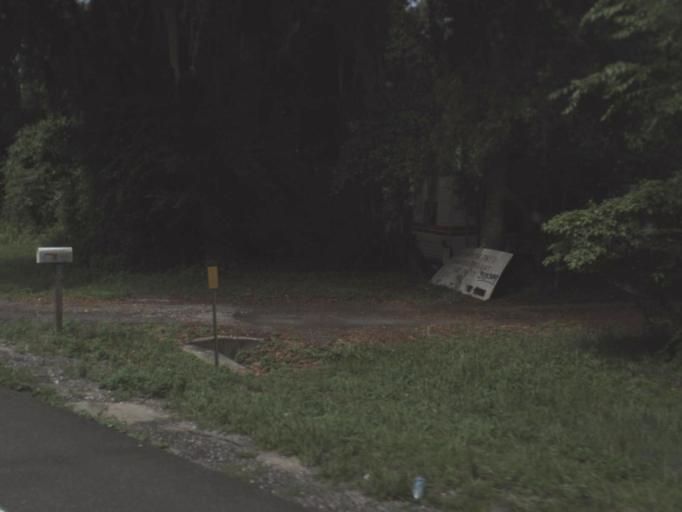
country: US
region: Florida
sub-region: Alachua County
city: Gainesville
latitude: 29.6544
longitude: -82.2585
